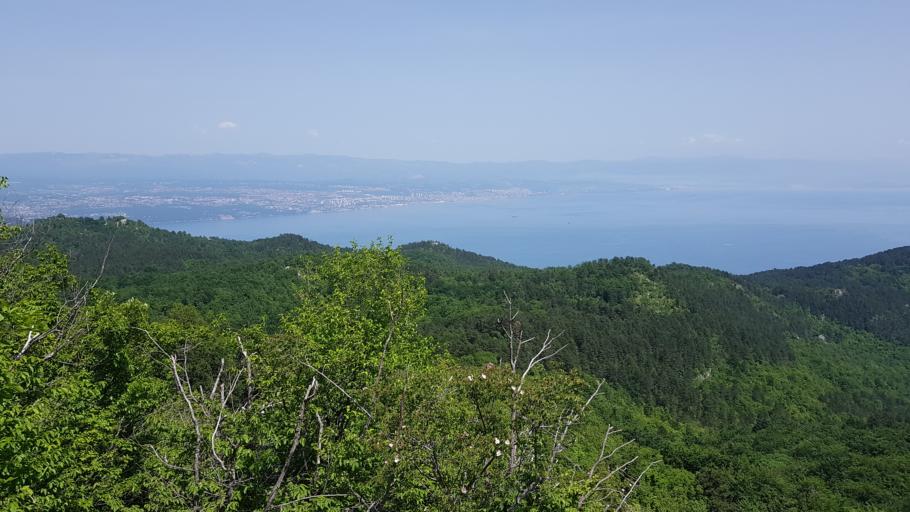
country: HR
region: Istarska
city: Lovran
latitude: 45.2883
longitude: 14.2283
